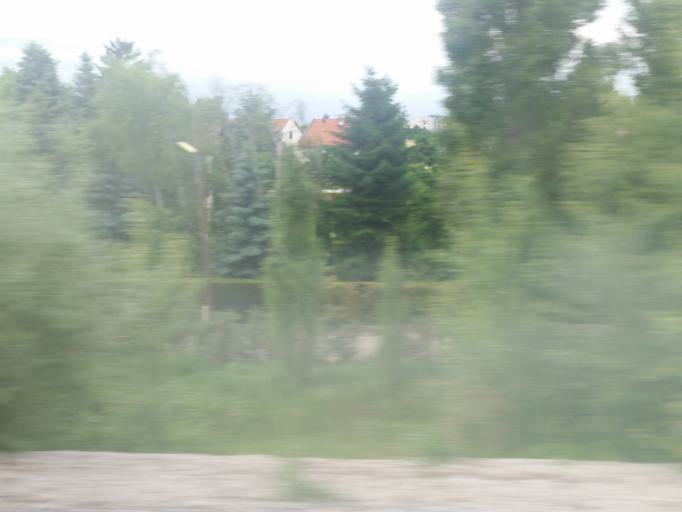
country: AT
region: Lower Austria
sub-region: Politischer Bezirk Wien-Umgebung
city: Gerasdorf bei Wien
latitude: 48.2337
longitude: 16.4833
